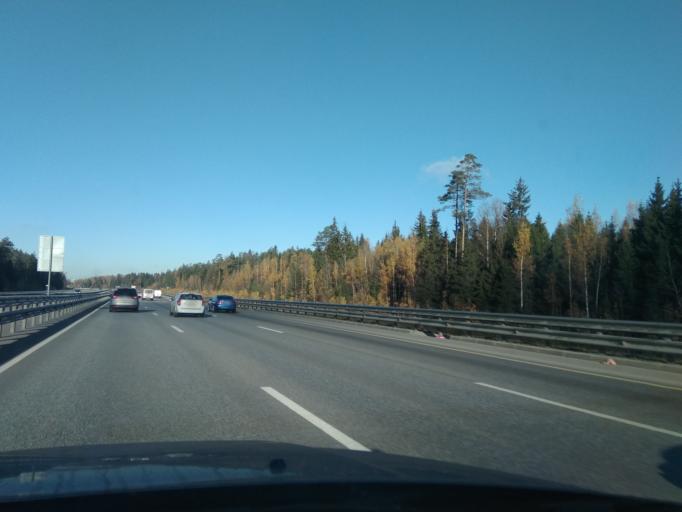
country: RU
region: Moskovskaya
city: Yershovo
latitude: 55.8414
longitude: 36.8309
